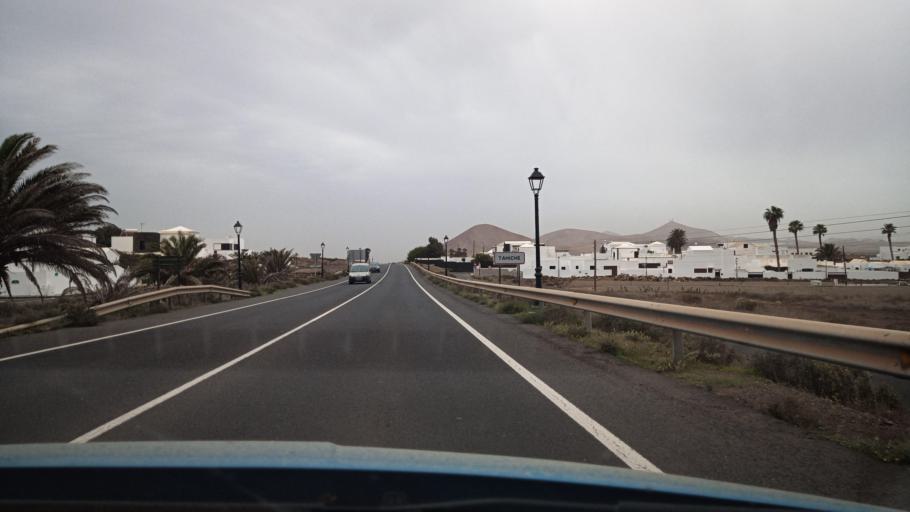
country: ES
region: Canary Islands
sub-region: Provincia de Las Palmas
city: Nazaret
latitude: 29.0185
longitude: -13.5400
